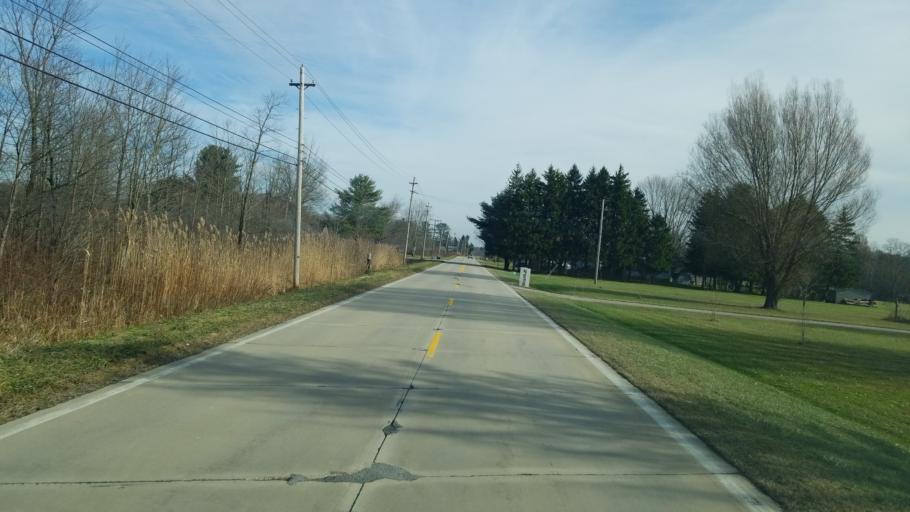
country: US
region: Ohio
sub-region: Ashtabula County
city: Roaming Shores
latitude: 41.6637
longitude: -80.8989
